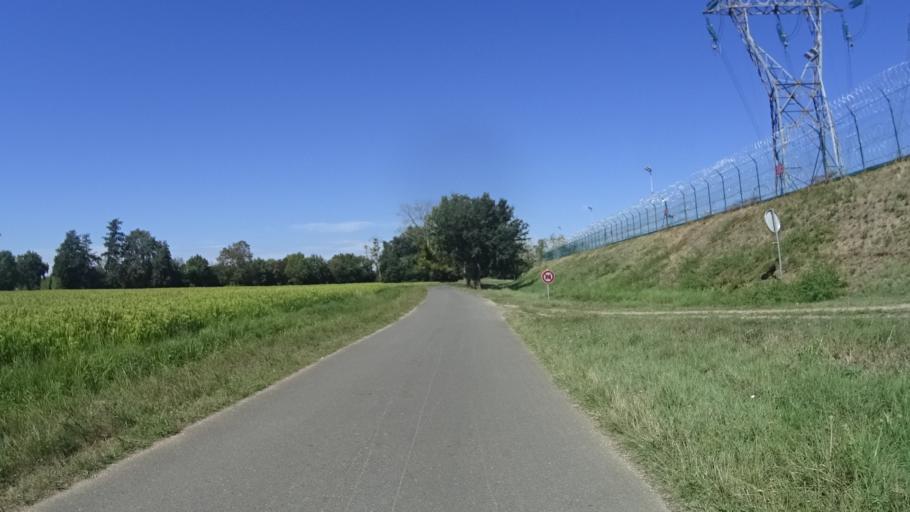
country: FR
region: Centre
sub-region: Departement du Cher
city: Belleville-sur-Loire
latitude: 47.5043
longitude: 2.8712
